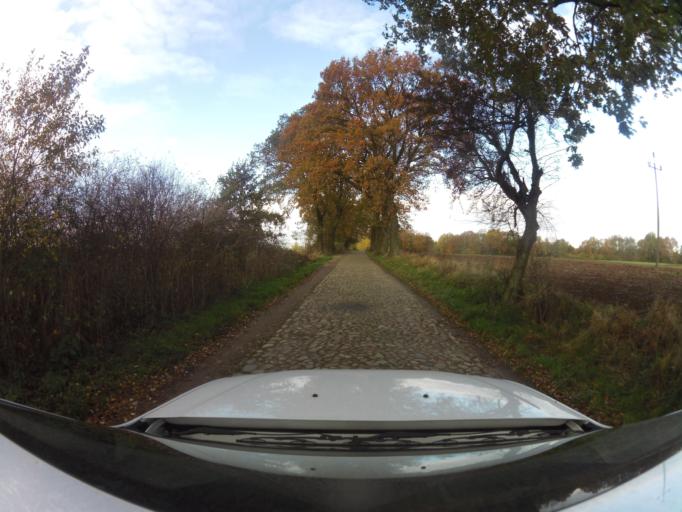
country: PL
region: West Pomeranian Voivodeship
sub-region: Powiat gryficki
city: Trzebiatow
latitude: 54.0461
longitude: 15.2188
